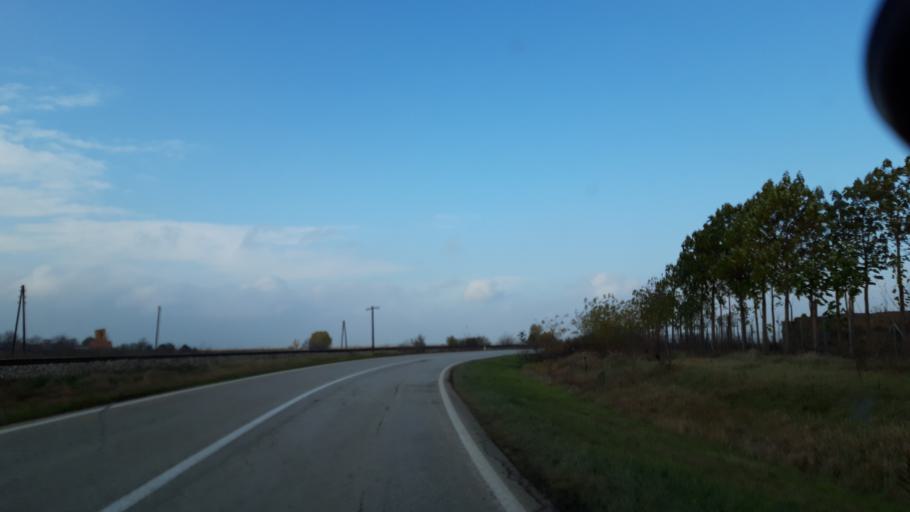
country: RS
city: Padej
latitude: 45.8337
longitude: 20.1663
